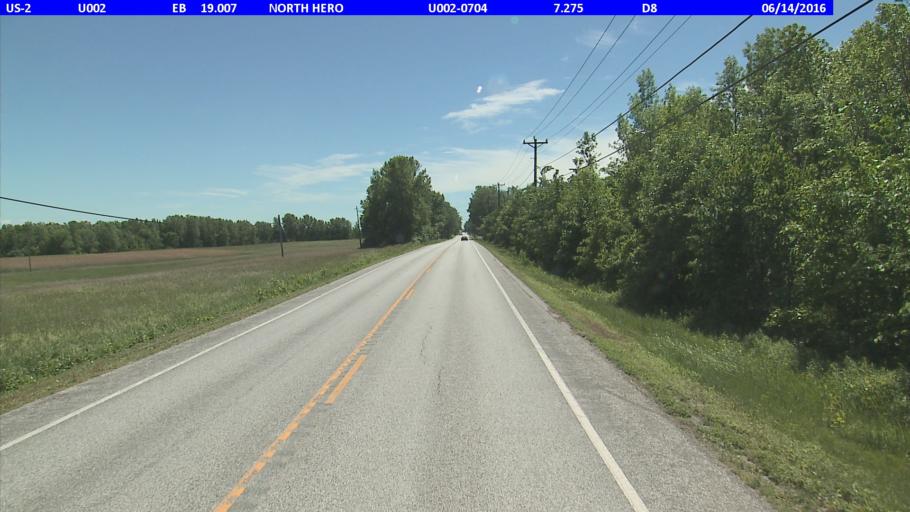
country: US
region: Vermont
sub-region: Grand Isle County
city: North Hero
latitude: 44.7948
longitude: -73.2925
